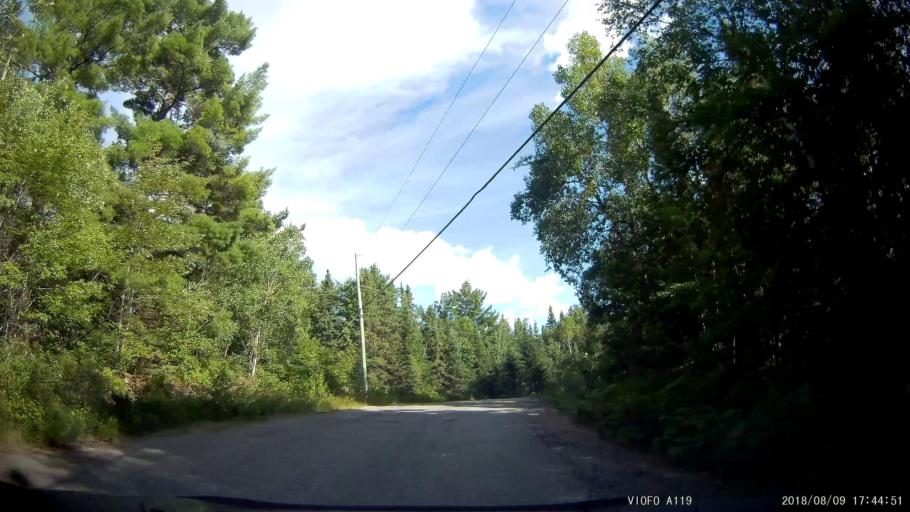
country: CA
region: Ontario
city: Rayside-Balfour
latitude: 46.6038
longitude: -81.5326
